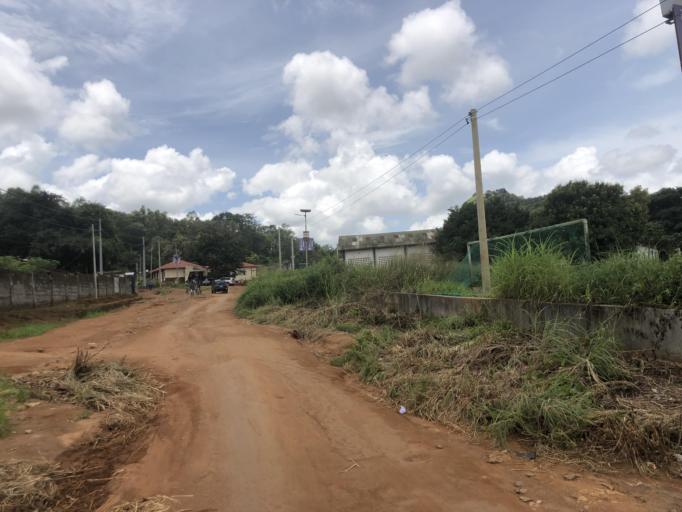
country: SL
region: Northern Province
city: Makeni
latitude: 8.8775
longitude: -12.0531
